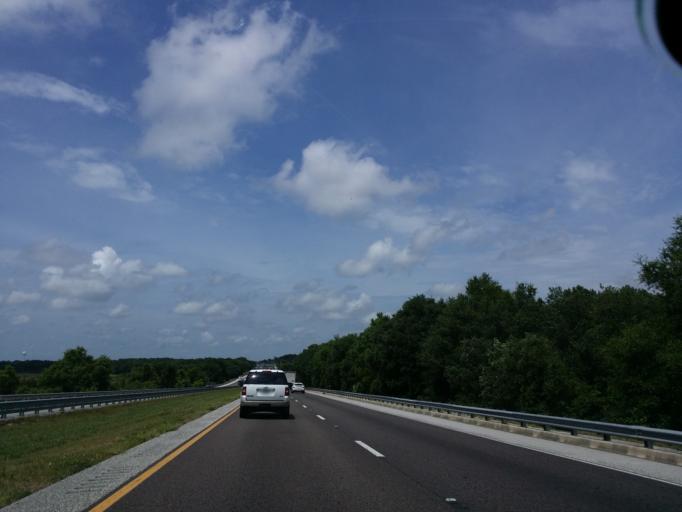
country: US
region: Florida
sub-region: Lake County
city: Minneola
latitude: 28.6191
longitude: -81.7454
